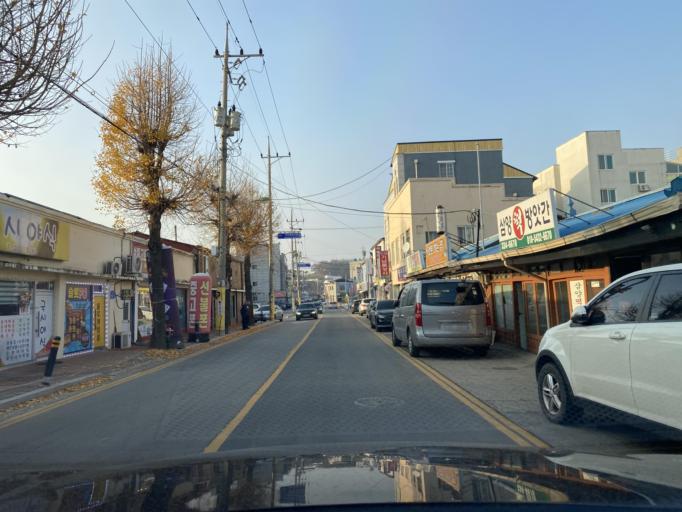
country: KR
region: Chungcheongnam-do
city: Yesan
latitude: 36.6880
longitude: 126.8309
